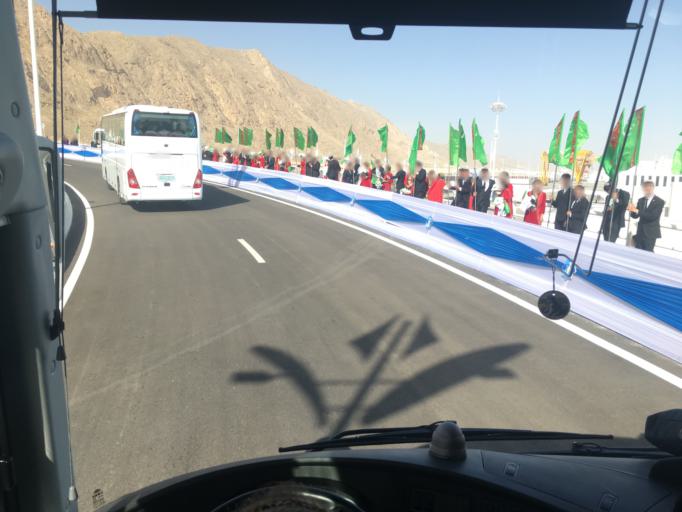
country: TM
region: Balkan
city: Turkmenbasy
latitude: 40.0057
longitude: 53.0237
